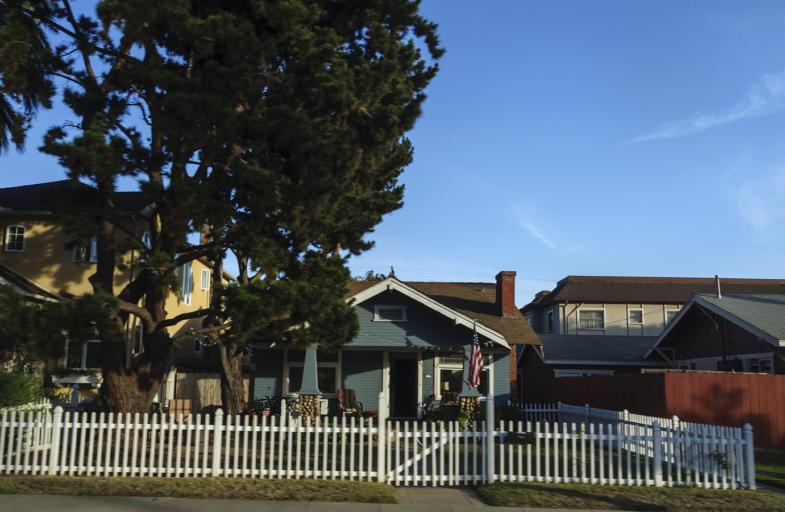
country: US
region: California
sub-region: San Diego County
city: Coronado
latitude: 32.6866
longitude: -117.1766
